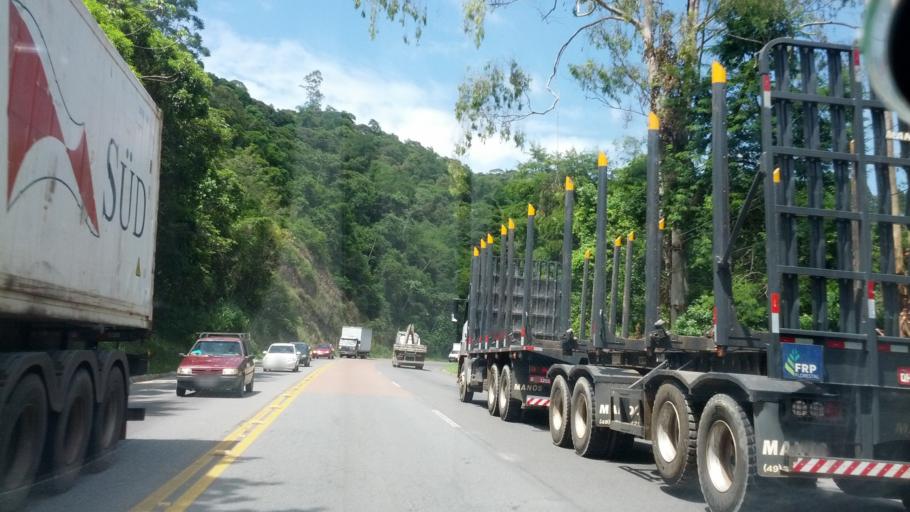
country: BR
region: Santa Catarina
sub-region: Ibirama
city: Ibirama
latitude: -27.0905
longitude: -49.5206
